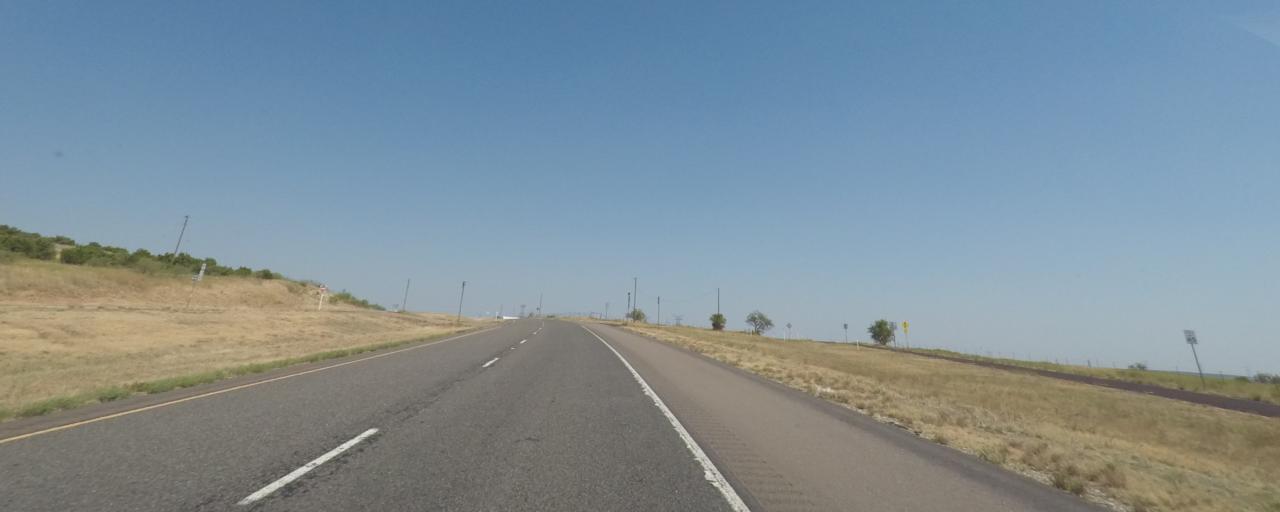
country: US
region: Texas
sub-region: Dickens County
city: Dickens
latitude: 33.6206
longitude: -100.8591
